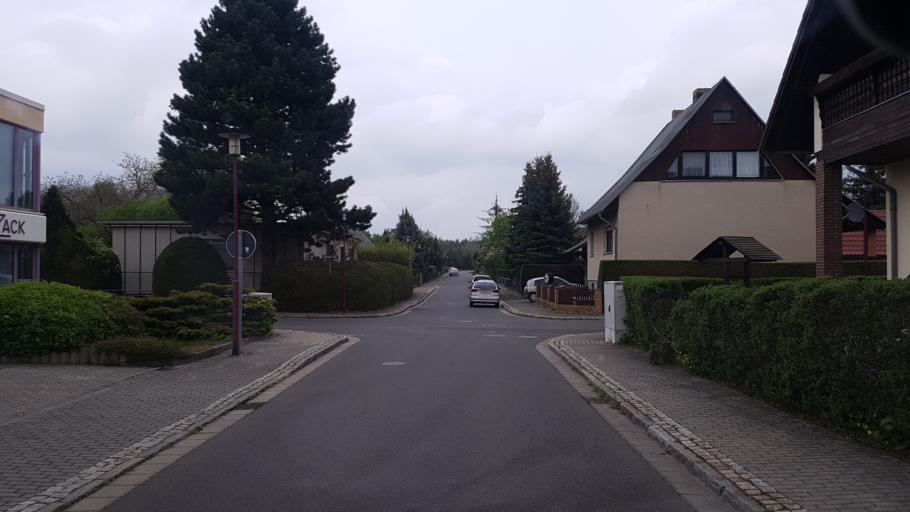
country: DE
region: Brandenburg
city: Grossraschen
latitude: 51.5841
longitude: 13.9661
